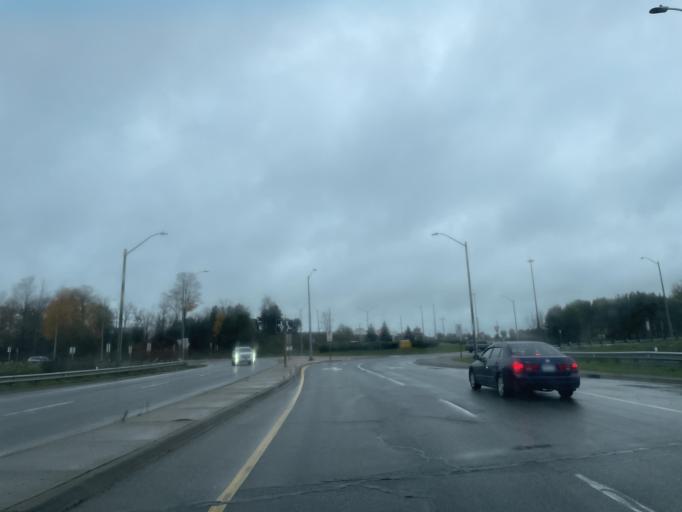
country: CA
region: Ontario
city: Cambridge
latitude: 43.4207
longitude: -80.3294
